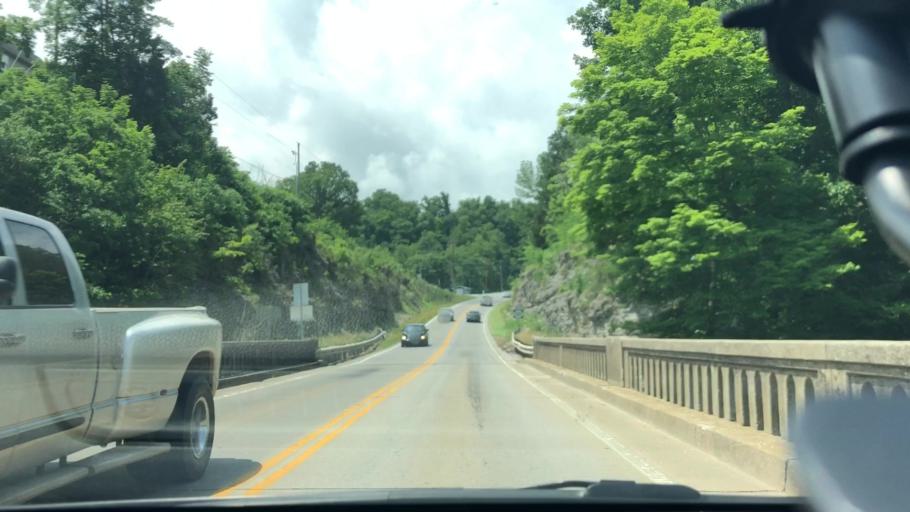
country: US
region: Kentucky
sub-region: Pulaski County
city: Somerset
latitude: 37.0506
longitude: -84.6798
